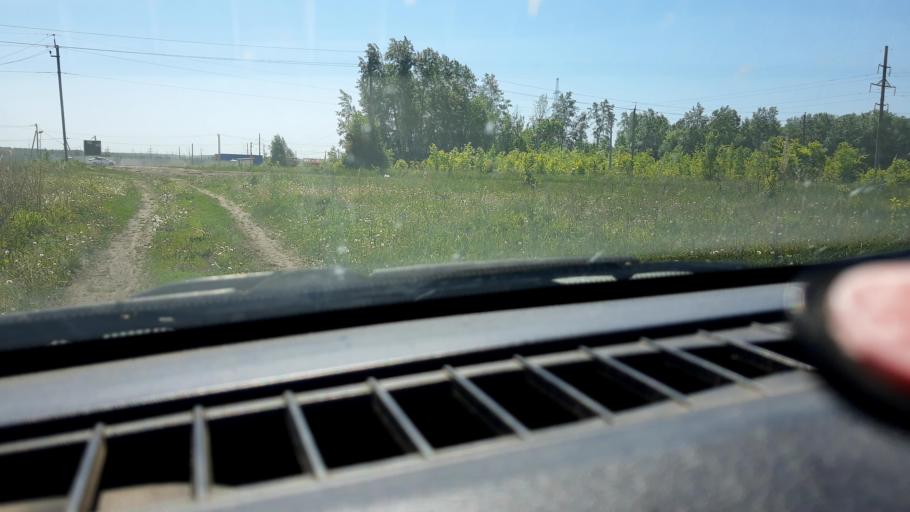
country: RU
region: Bashkortostan
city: Kabakovo
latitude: 54.6810
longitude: 56.1080
